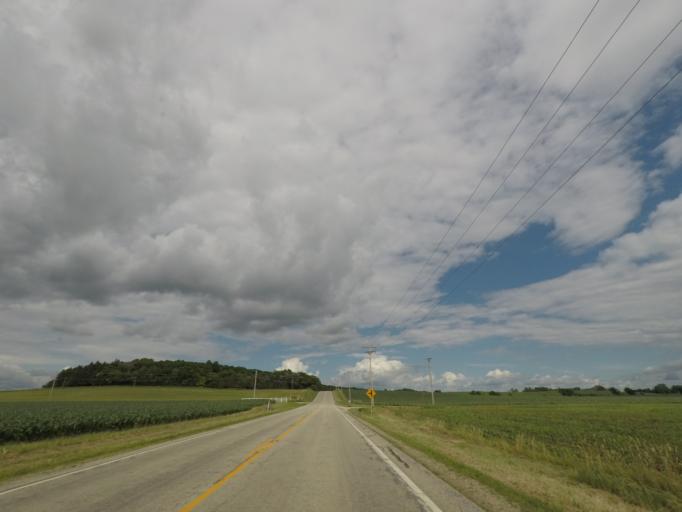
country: US
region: Wisconsin
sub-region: Dane County
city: Belleville
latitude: 42.8281
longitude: -89.4755
